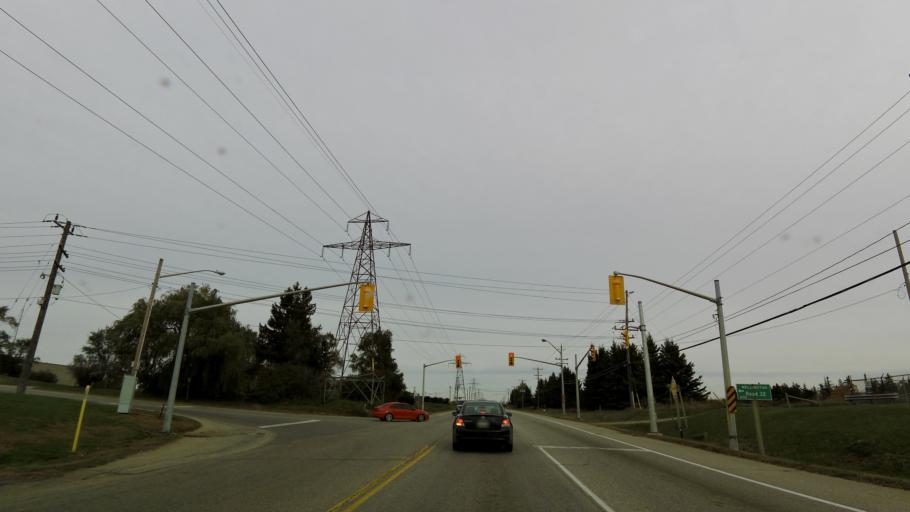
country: CA
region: Ontario
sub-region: Wellington County
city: Guelph
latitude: 43.4904
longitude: -80.2844
